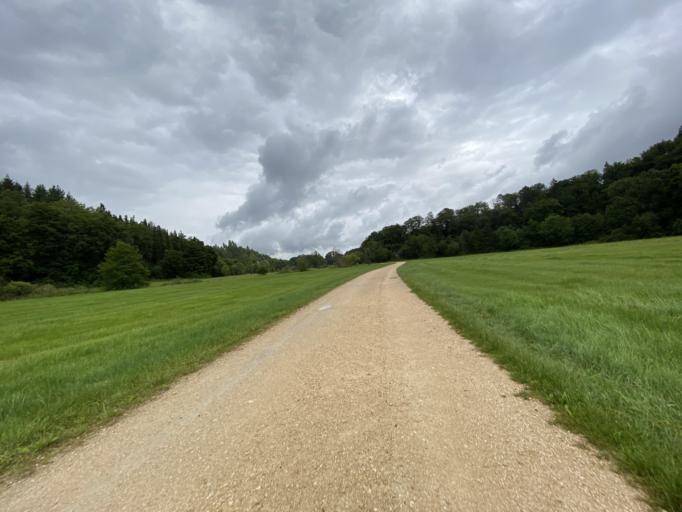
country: DE
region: Baden-Wuerttemberg
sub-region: Tuebingen Region
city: Sigmaringen
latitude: 48.1033
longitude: 9.2450
